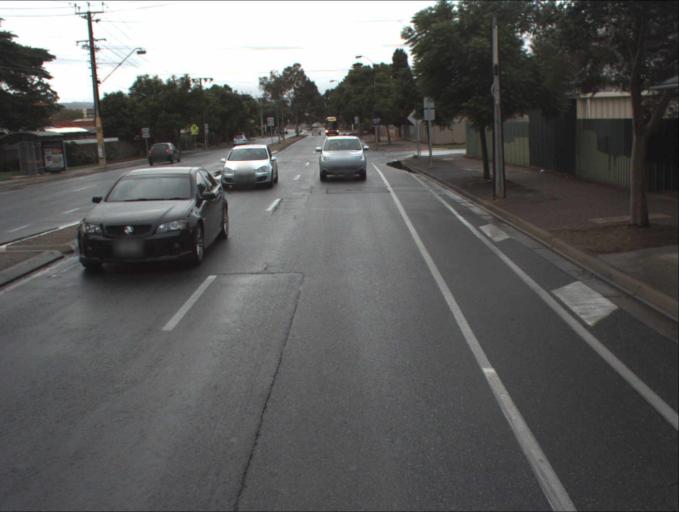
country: AU
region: South Australia
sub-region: Norwood Payneham St Peters
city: Marden
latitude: -34.8884
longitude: 138.6395
